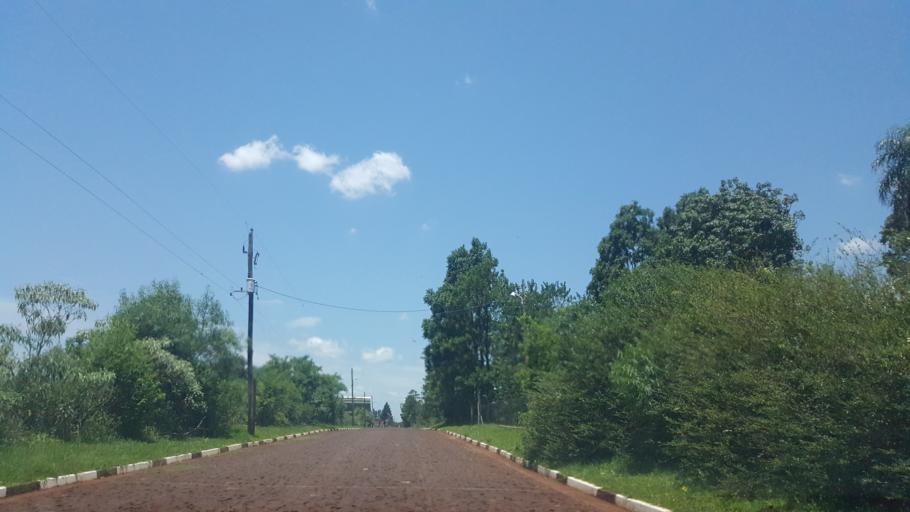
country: AR
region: Misiones
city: Garupa
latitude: -27.4965
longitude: -55.8568
